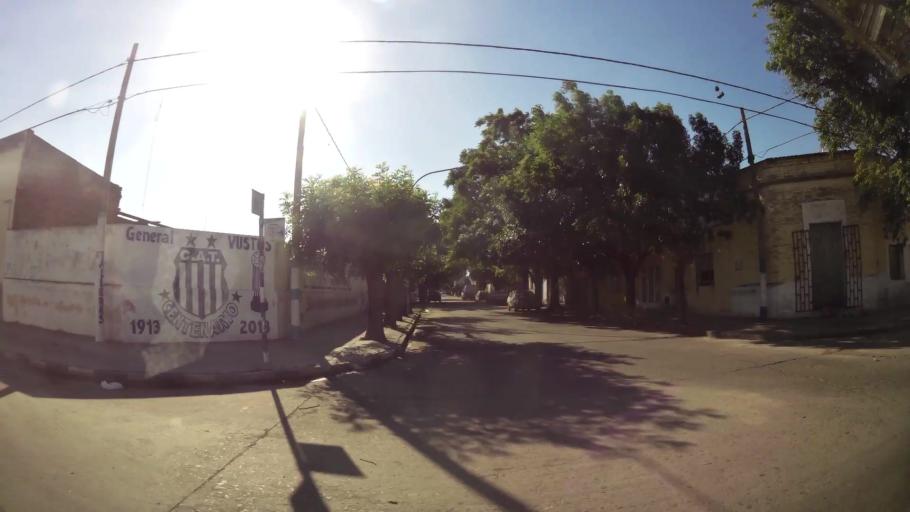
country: AR
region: Cordoba
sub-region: Departamento de Capital
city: Cordoba
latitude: -31.3931
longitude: -64.1684
